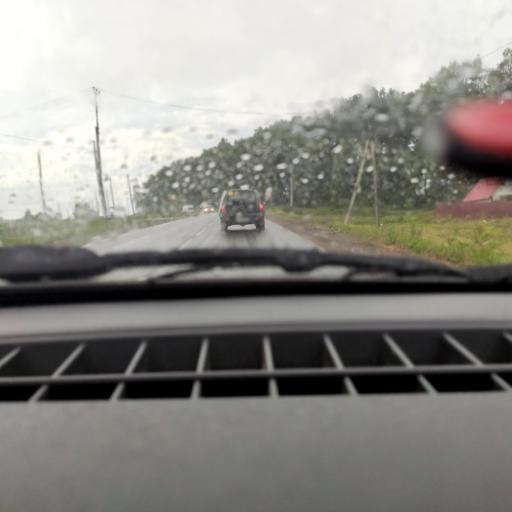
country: RU
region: Bashkortostan
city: Kabakovo
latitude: 54.5940
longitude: 56.2342
